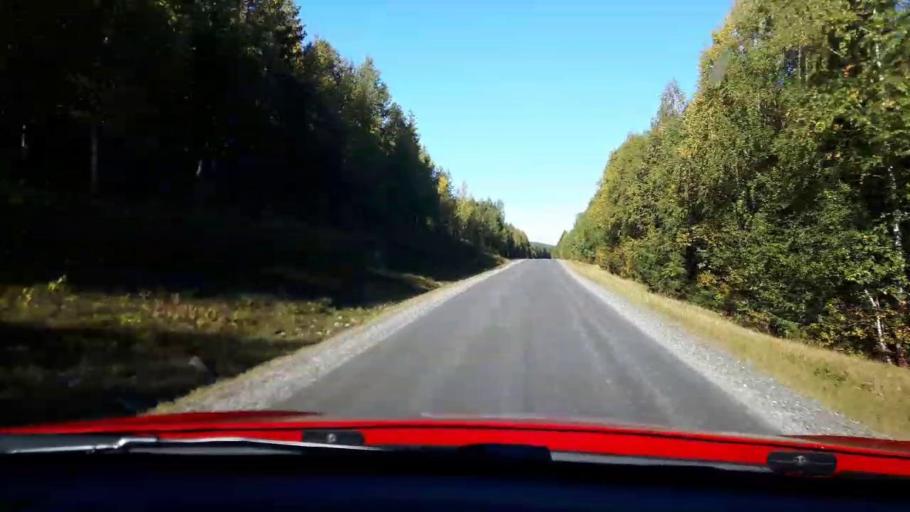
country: NO
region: Nord-Trondelag
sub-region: Lierne
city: Sandvika
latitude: 64.5344
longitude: 14.0231
